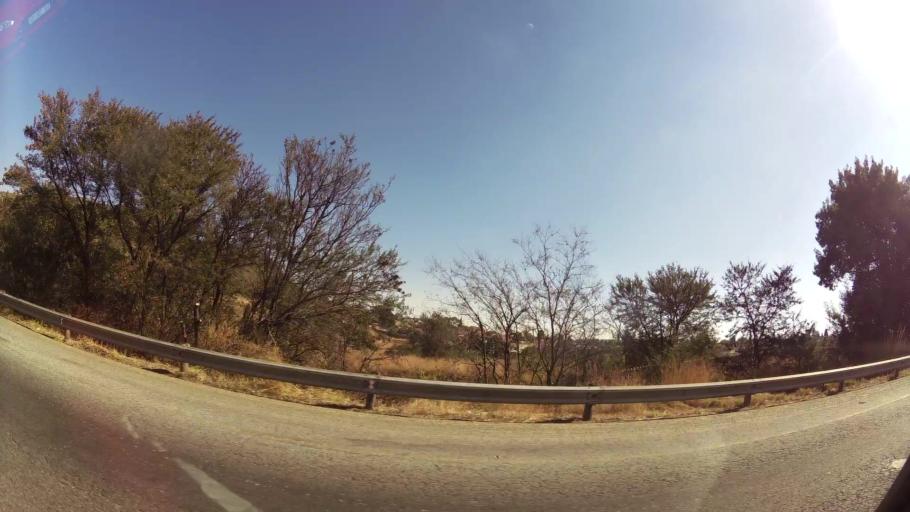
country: ZA
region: Gauteng
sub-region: City of Johannesburg Metropolitan Municipality
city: Johannesburg
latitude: -26.2797
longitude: 28.0337
